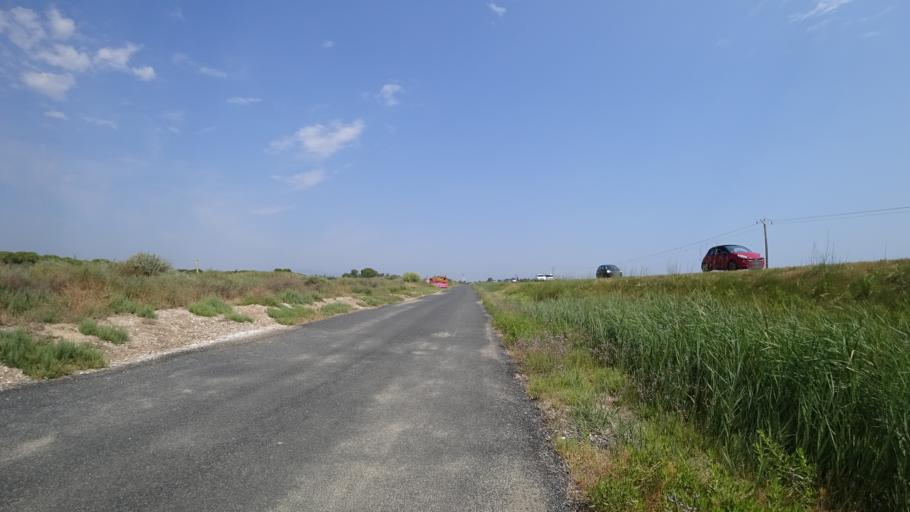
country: FR
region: Languedoc-Roussillon
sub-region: Departement des Pyrenees-Orientales
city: Torreilles
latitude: 42.7543
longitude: 3.0208
